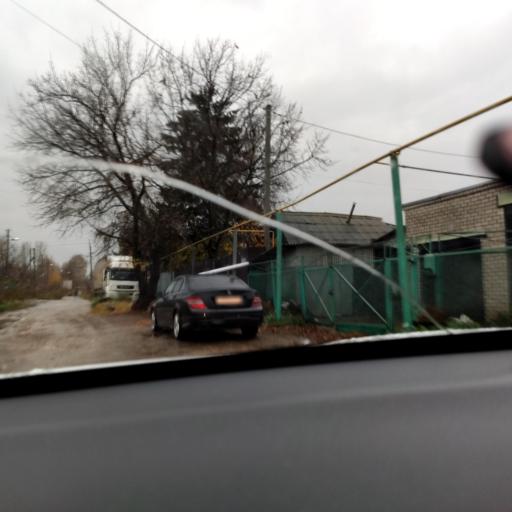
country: RU
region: Tatarstan
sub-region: Gorod Kazan'
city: Kazan
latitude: 55.8680
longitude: 49.1092
